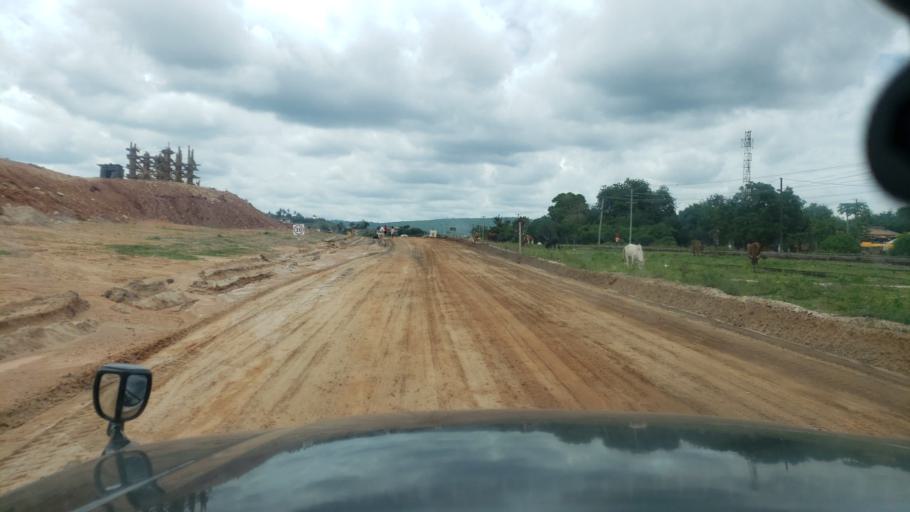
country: TZ
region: Pwani
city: Kisarawe
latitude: -6.8852
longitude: 39.1445
